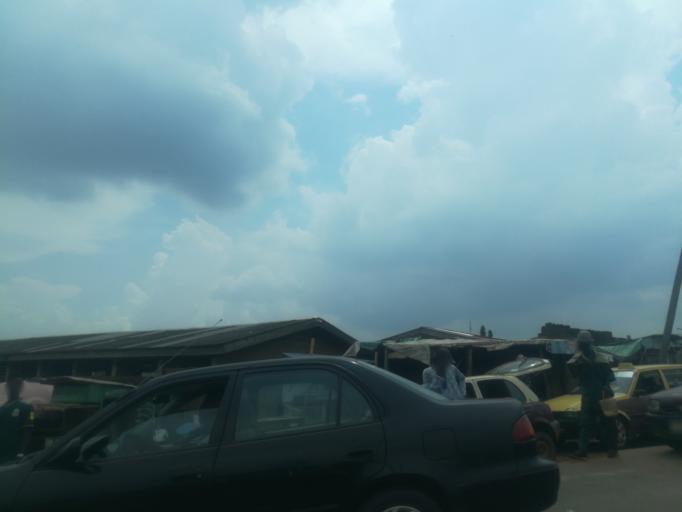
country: NG
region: Oyo
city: Ibadan
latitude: 7.4305
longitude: 3.9132
